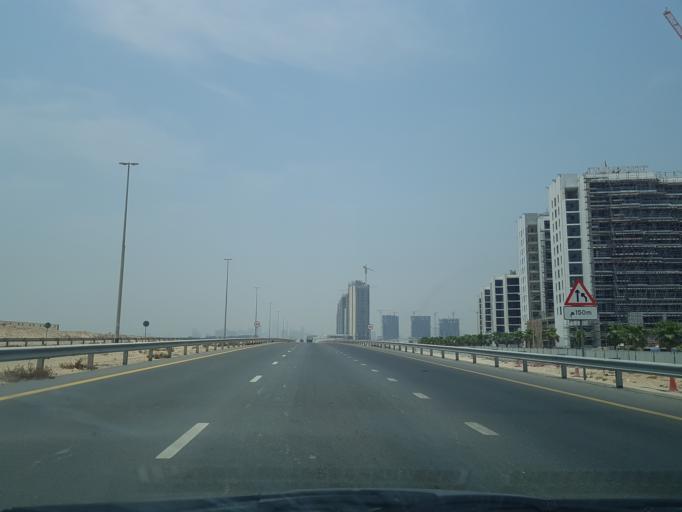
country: AE
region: Dubai
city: Dubai
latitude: 25.0116
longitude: 55.2515
